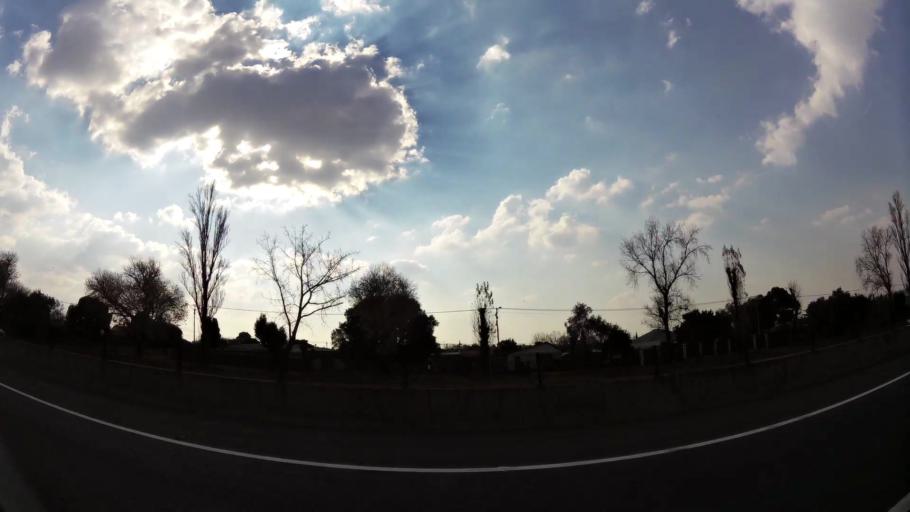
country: ZA
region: Gauteng
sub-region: Ekurhuleni Metropolitan Municipality
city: Germiston
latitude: -26.2545
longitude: 28.1938
